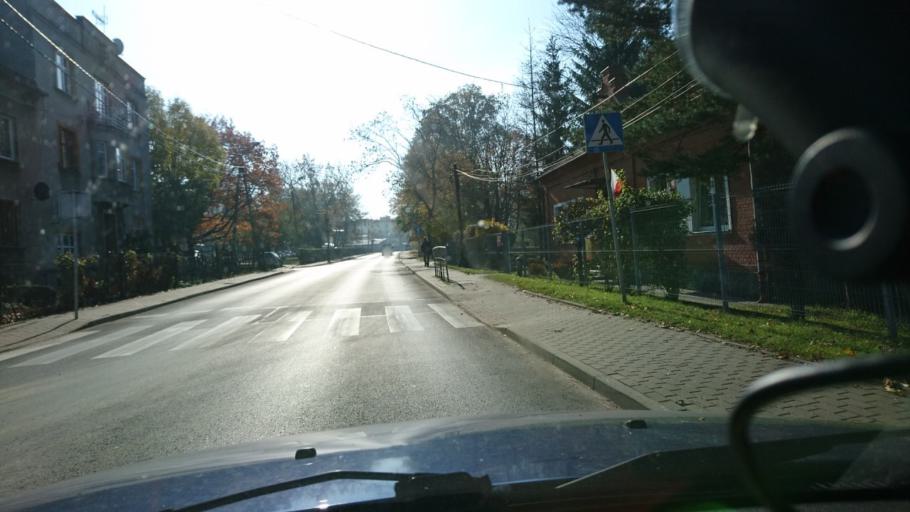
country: PL
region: Silesian Voivodeship
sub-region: Bielsko-Biala
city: Bielsko-Biala
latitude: 49.8133
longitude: 19.0472
